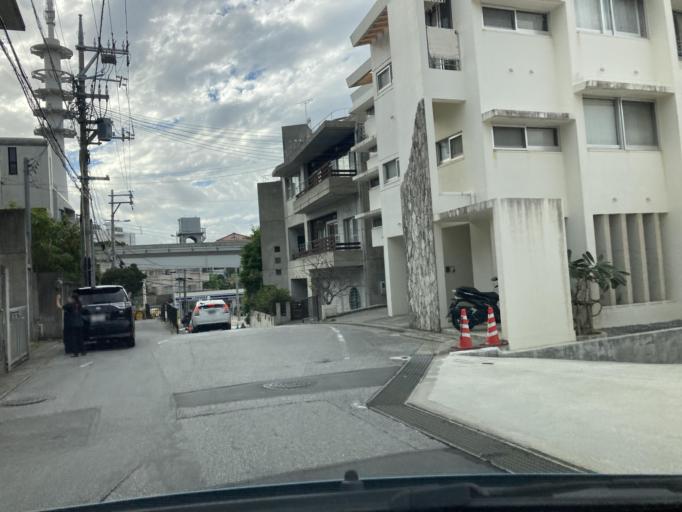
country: JP
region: Okinawa
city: Naha-shi
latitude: 26.2215
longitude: 127.7276
